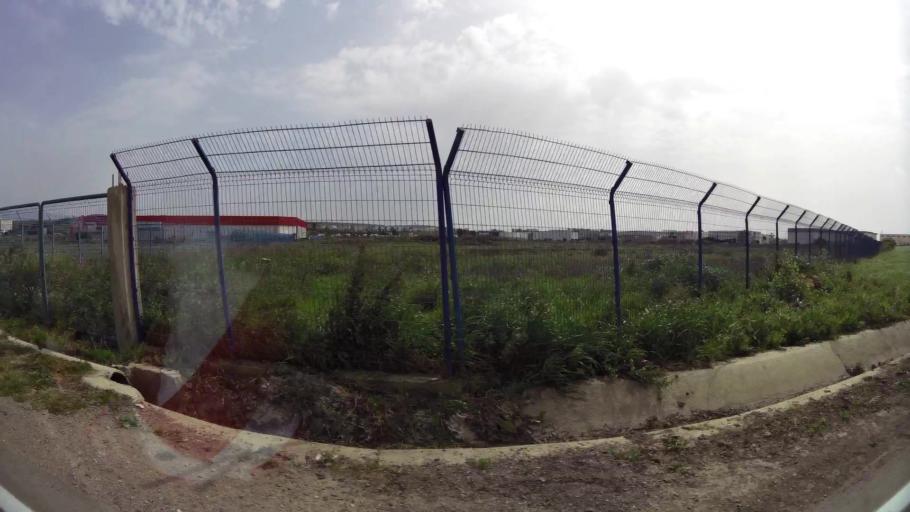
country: MA
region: Tanger-Tetouan
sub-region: Tanger-Assilah
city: Boukhalef
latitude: 35.7272
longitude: -5.8972
